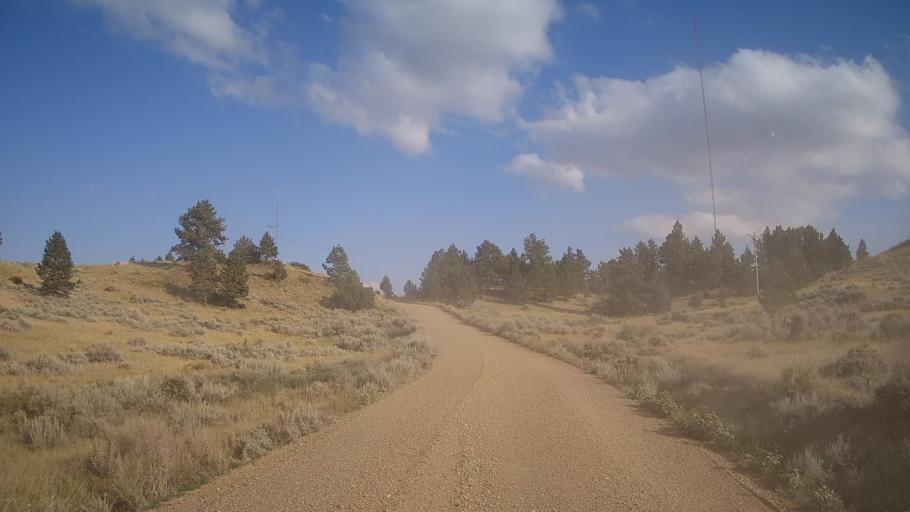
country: US
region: Montana
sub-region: Dawson County
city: Glendive
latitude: 47.0539
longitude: -104.6791
